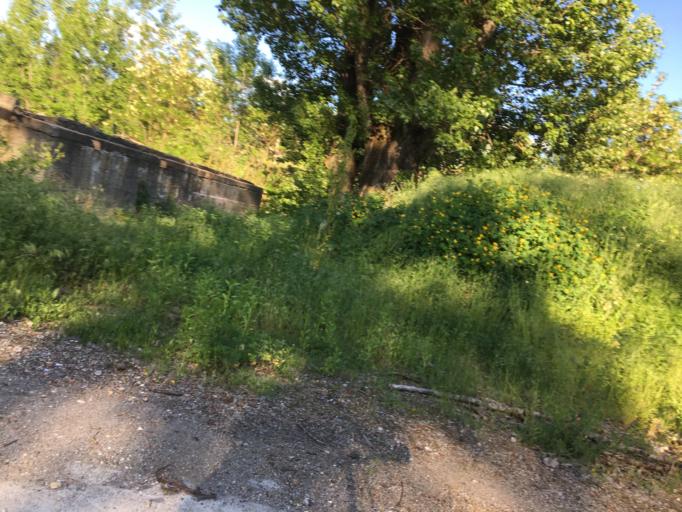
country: HU
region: Budapest
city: Budapest III. keruelet
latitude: 47.5413
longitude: 19.0510
